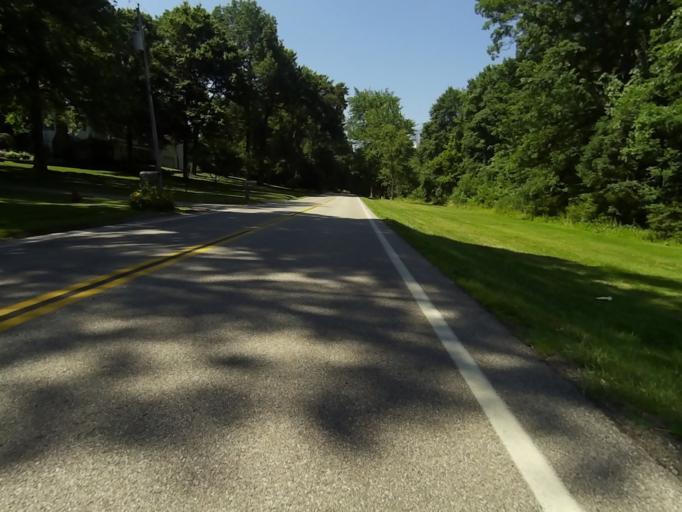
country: US
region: Ohio
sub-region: Portage County
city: Kent
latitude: 41.1567
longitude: -81.3707
